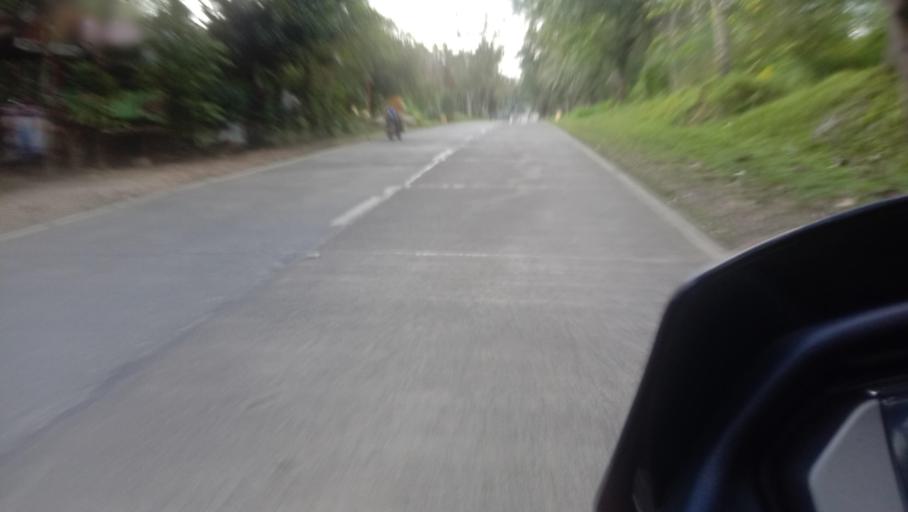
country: PH
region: Caraga
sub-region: Province of Surigao del Sur
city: Barobo
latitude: 8.5159
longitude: 126.1245
